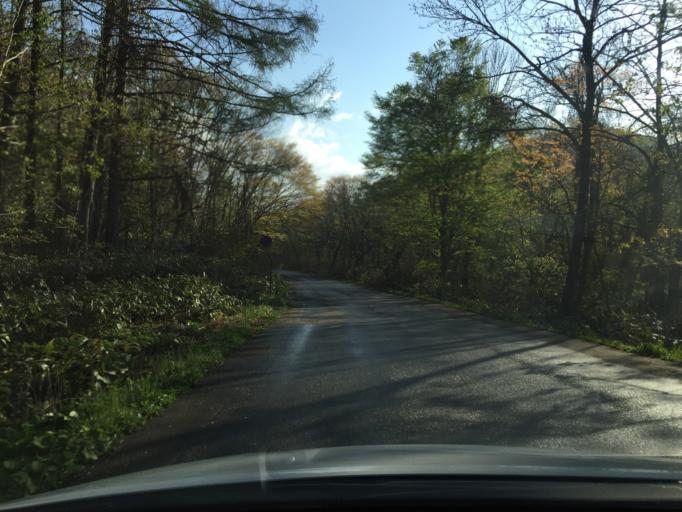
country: JP
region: Fukushima
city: Inawashiro
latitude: 37.6453
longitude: 140.0347
